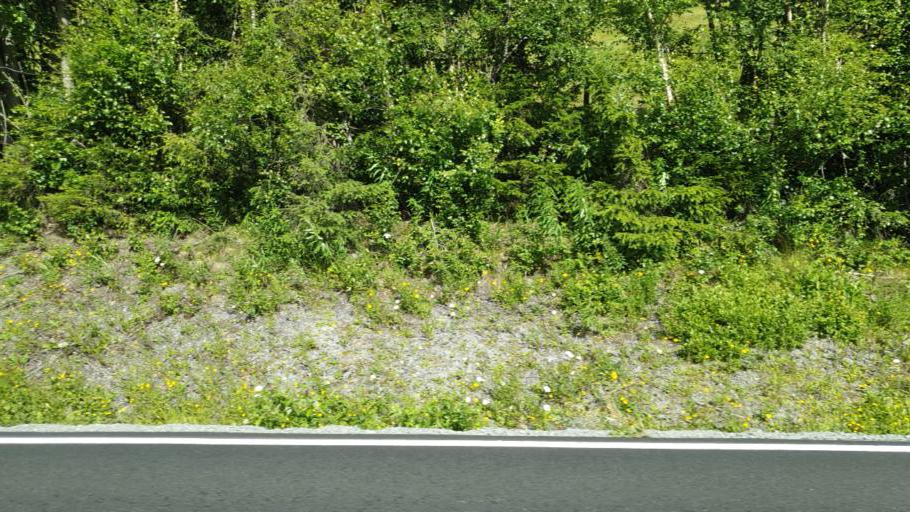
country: NO
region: Oppland
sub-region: Oystre Slidre
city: Heggenes
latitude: 61.1683
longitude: 8.9956
